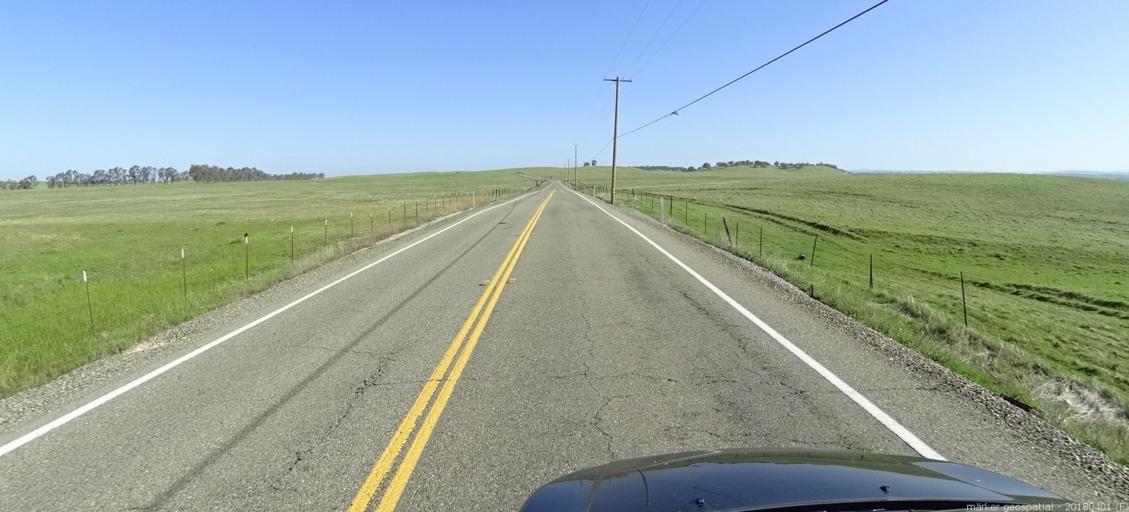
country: US
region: California
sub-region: Sacramento County
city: Rancho Murieta
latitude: 38.4320
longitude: -121.0501
